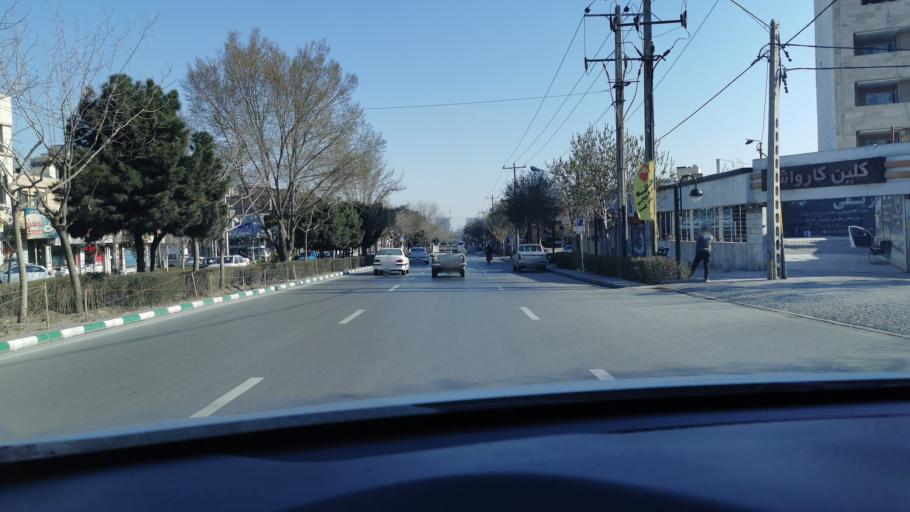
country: IR
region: Razavi Khorasan
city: Mashhad
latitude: 36.2646
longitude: 59.5857
